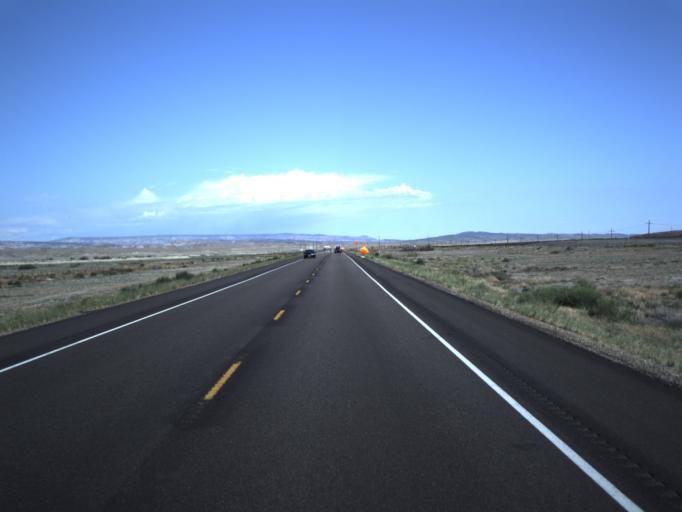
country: US
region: Utah
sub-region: Carbon County
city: East Carbon City
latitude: 39.0150
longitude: -110.2872
